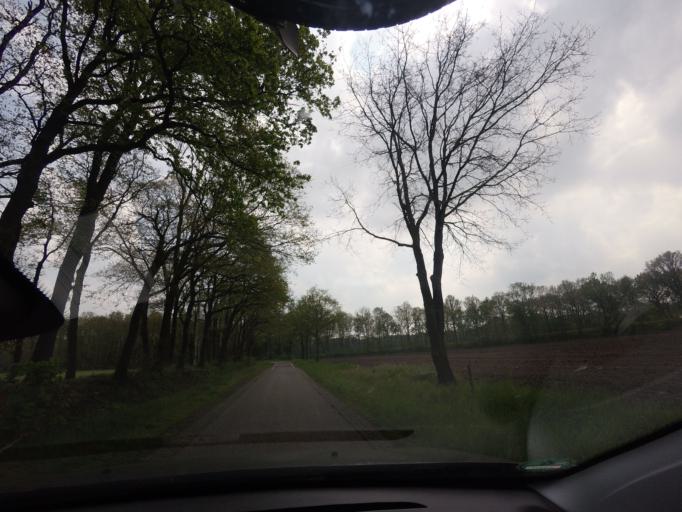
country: NL
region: Gelderland
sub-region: Oost Gelre
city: Lichtenvoorde
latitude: 52.0111
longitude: 6.6062
